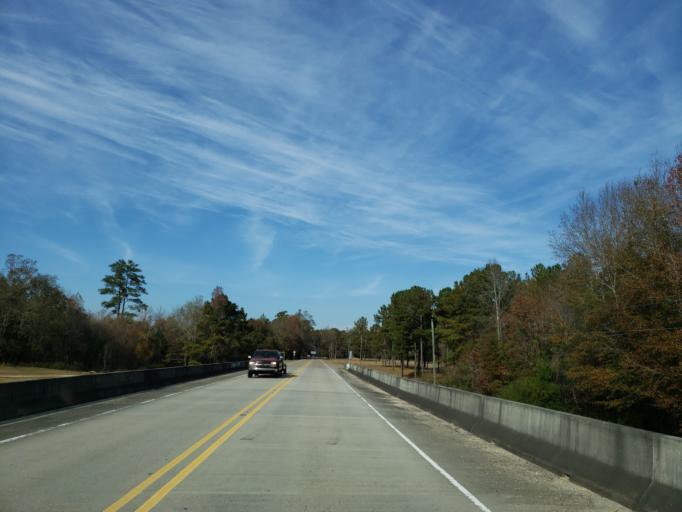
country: US
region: Mississippi
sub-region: Forrest County
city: Rawls Springs
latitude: 31.3968
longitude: -89.3651
